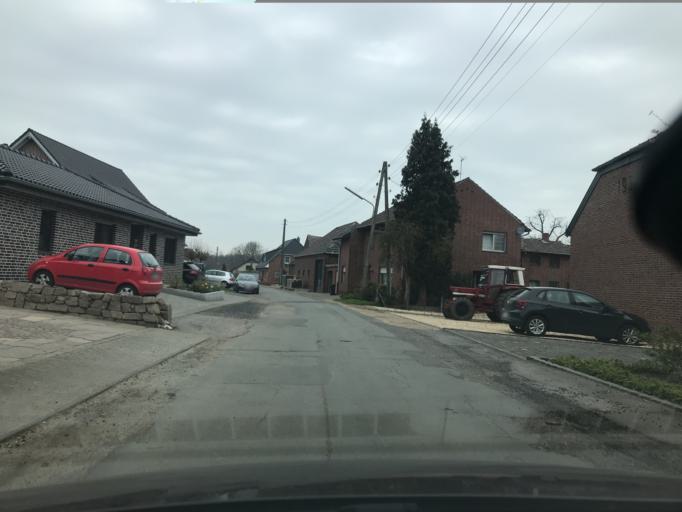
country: DE
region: North Rhine-Westphalia
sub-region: Regierungsbezirk Dusseldorf
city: Schwalmtal
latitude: 51.2366
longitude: 6.2334
